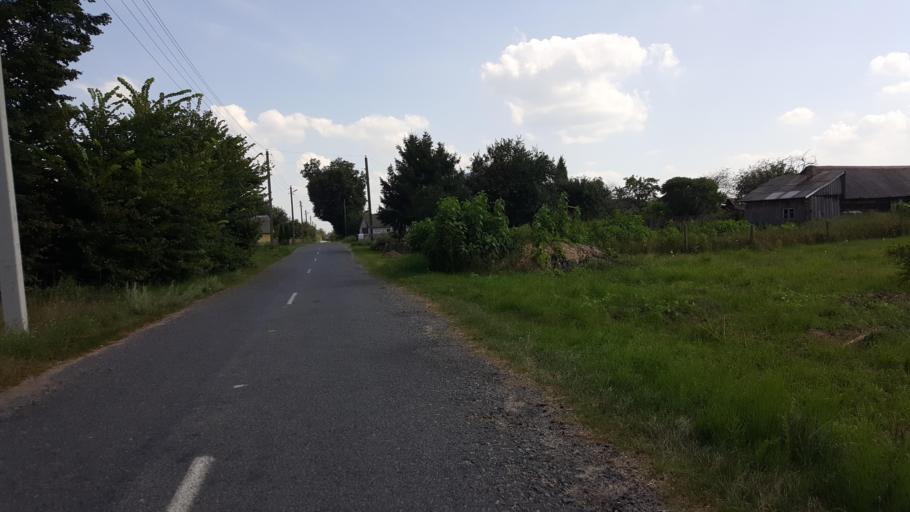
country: PL
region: Podlasie
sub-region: Powiat hajnowski
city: Czeremcha
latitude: 52.5131
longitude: 23.5434
